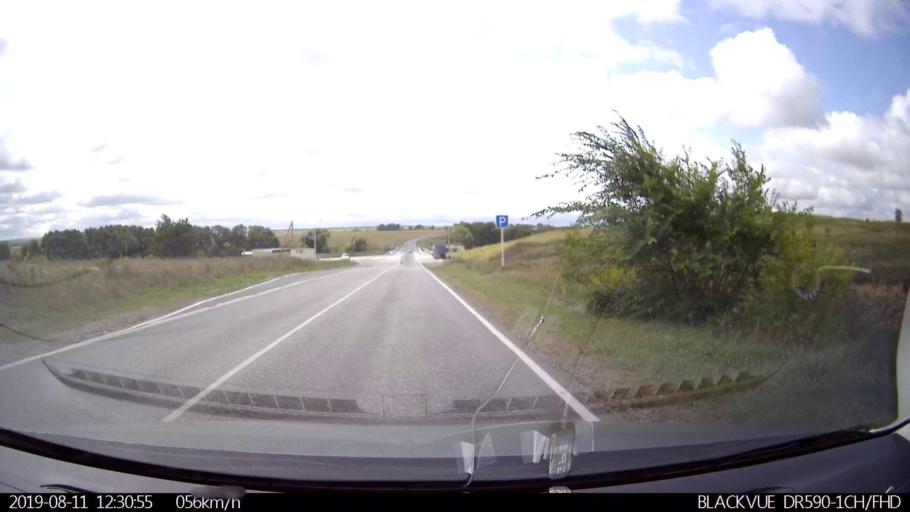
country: RU
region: Ulyanovsk
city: Ignatovka
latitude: 53.8225
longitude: 47.8885
